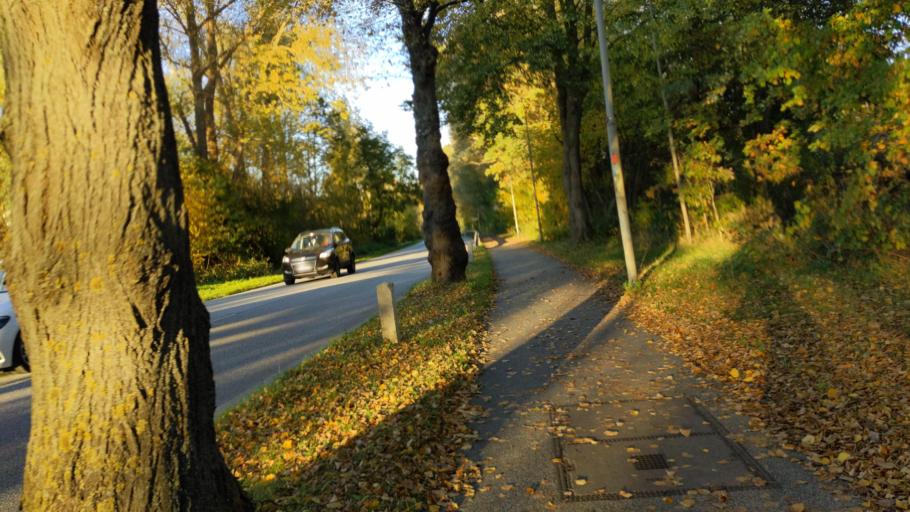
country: DE
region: Schleswig-Holstein
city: Luebeck
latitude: 53.8663
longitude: 10.7320
